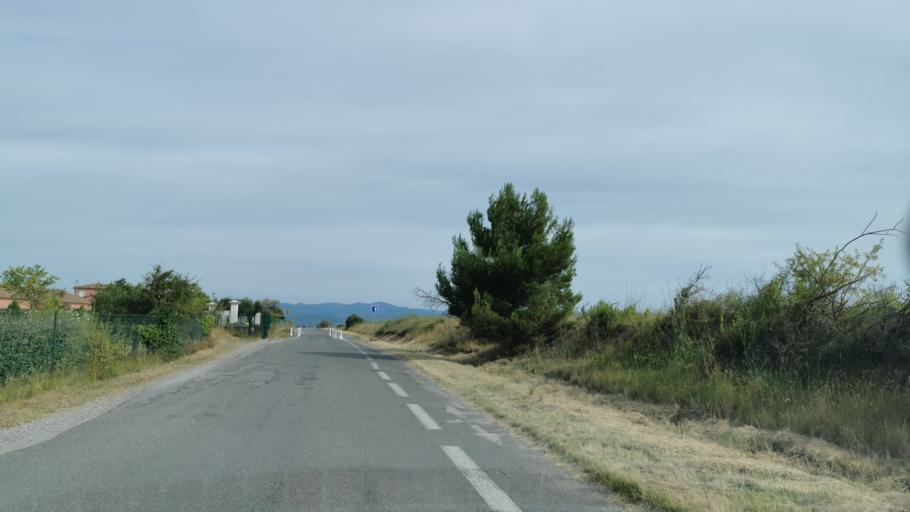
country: FR
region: Languedoc-Roussillon
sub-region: Departement de l'Herault
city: Olonzac
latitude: 43.2730
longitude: 2.7124
